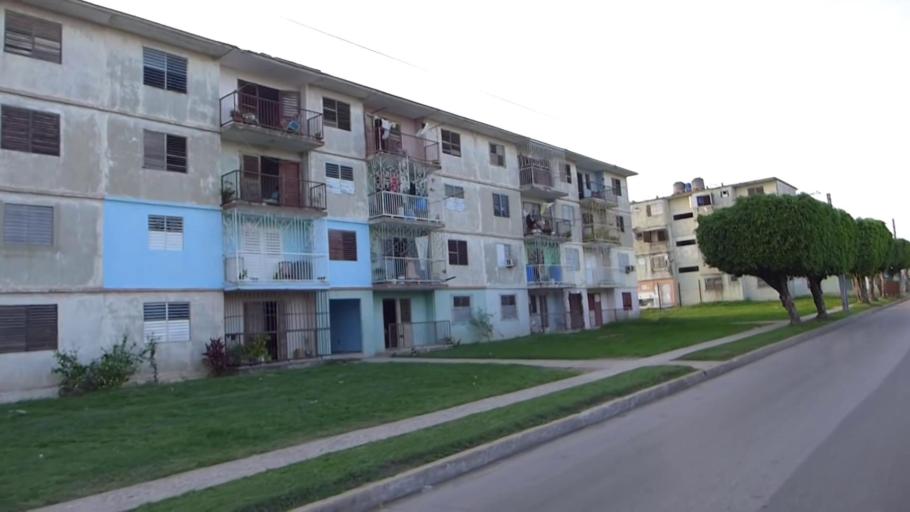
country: CU
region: Camaguey
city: Camaguey
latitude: 21.3804
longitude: -77.9369
